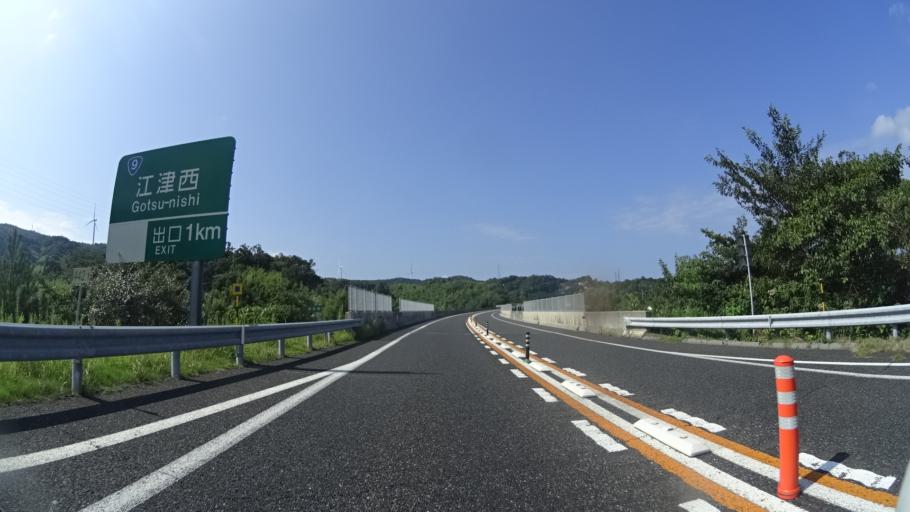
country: JP
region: Shimane
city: Gotsucho
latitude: 34.9735
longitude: 132.1926
